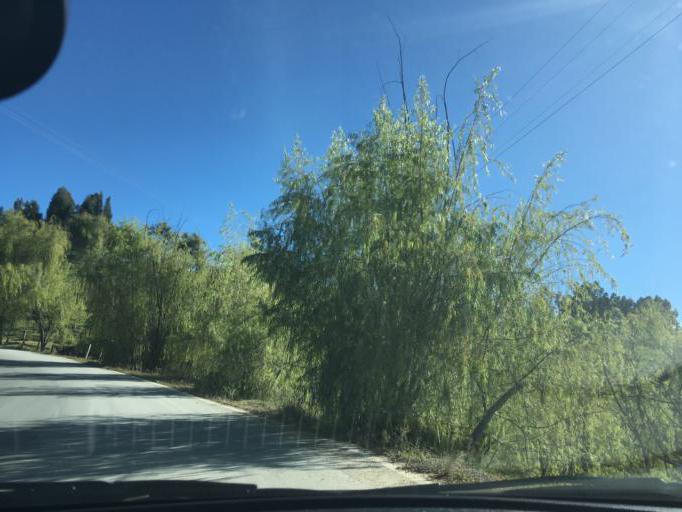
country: CO
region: Boyaca
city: Firavitoba
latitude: 5.5970
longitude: -72.9785
